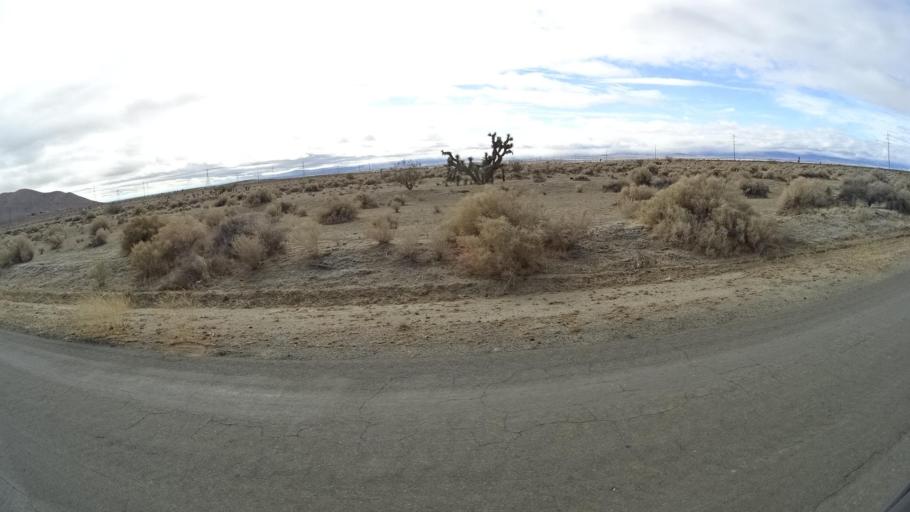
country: US
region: California
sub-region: Kern County
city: Rosamond
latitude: 34.8927
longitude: -118.3083
